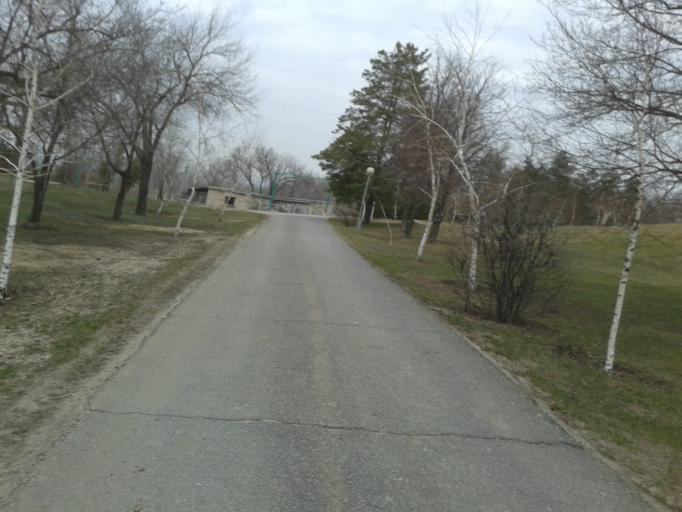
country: RU
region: Volgograd
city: Volgograd
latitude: 48.7426
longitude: 44.5364
